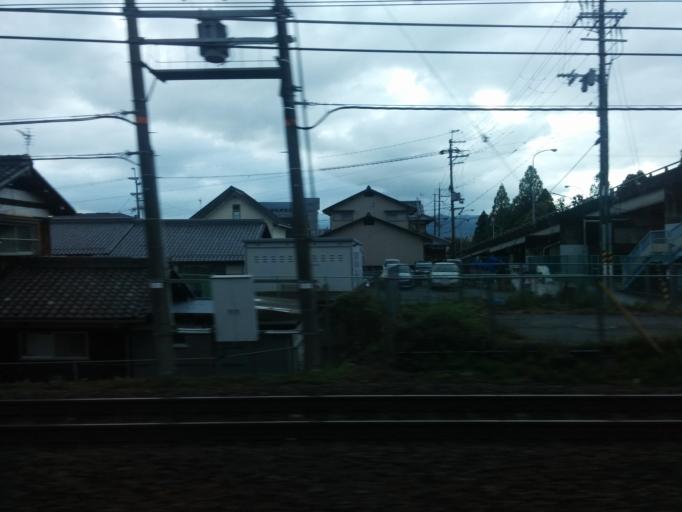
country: JP
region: Shiga Prefecture
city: Kusatsu
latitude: 35.0146
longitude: 135.9554
